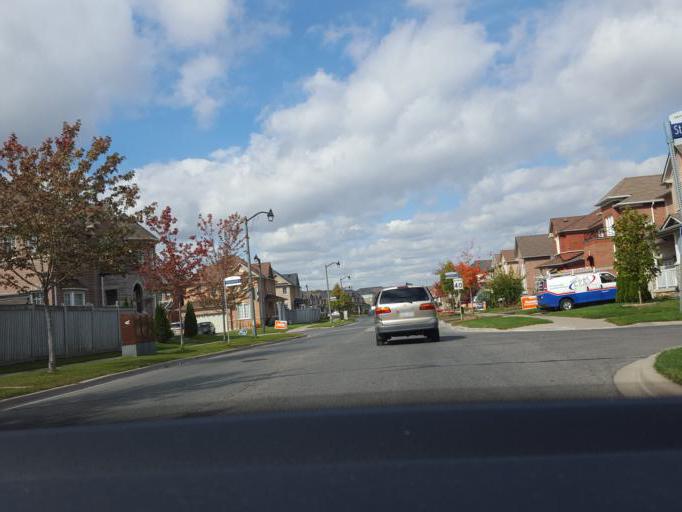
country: CA
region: Ontario
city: Markham
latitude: 43.8374
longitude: -79.2317
